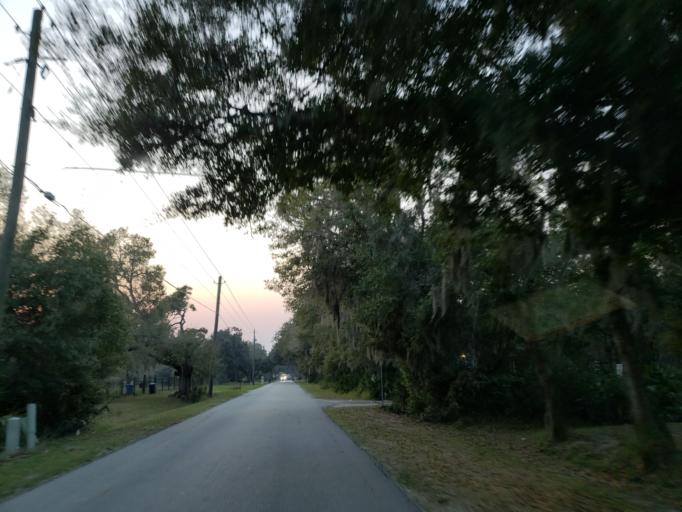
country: US
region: Florida
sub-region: Hillsborough County
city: Fish Hawk
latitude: 27.8428
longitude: -82.1968
